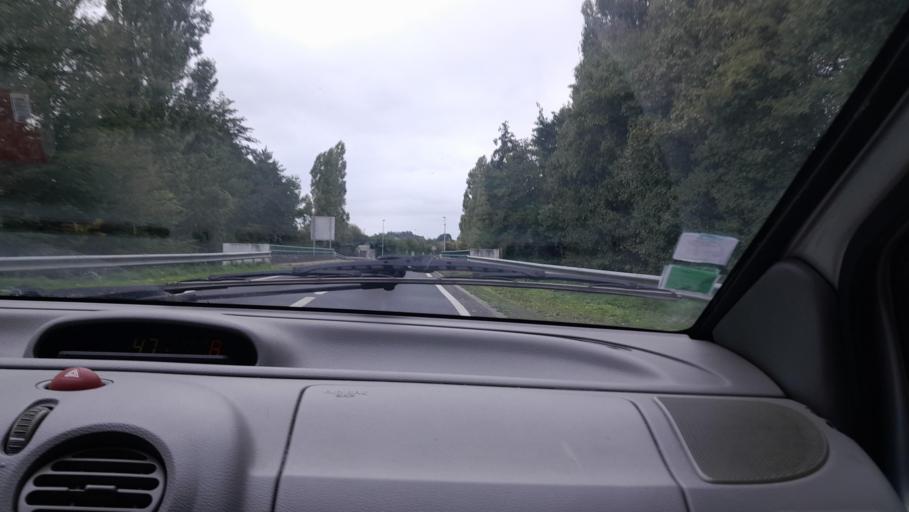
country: FR
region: Pays de la Loire
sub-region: Departement de la Loire-Atlantique
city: Saint-Mars-la-Jaille
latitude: 47.5259
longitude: -1.1768
